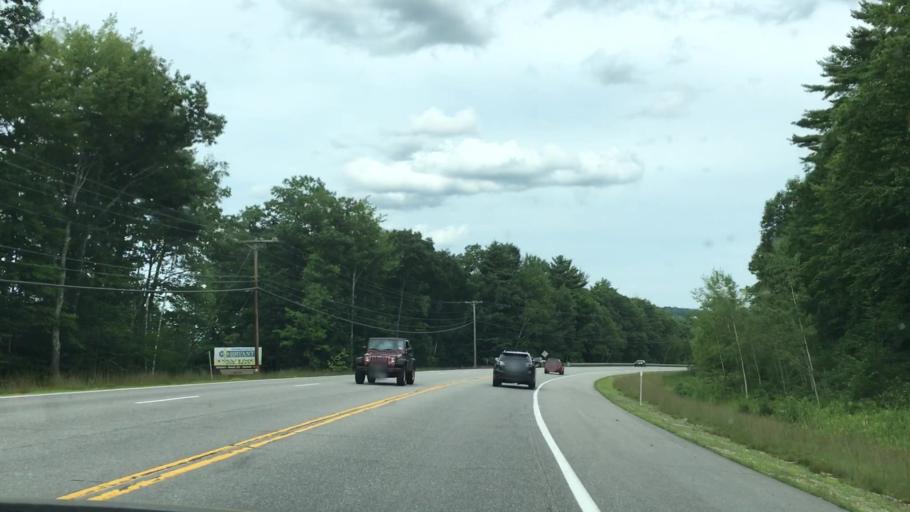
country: US
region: New Hampshire
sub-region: Belknap County
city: Meredith
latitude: 43.6426
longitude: -71.5209
